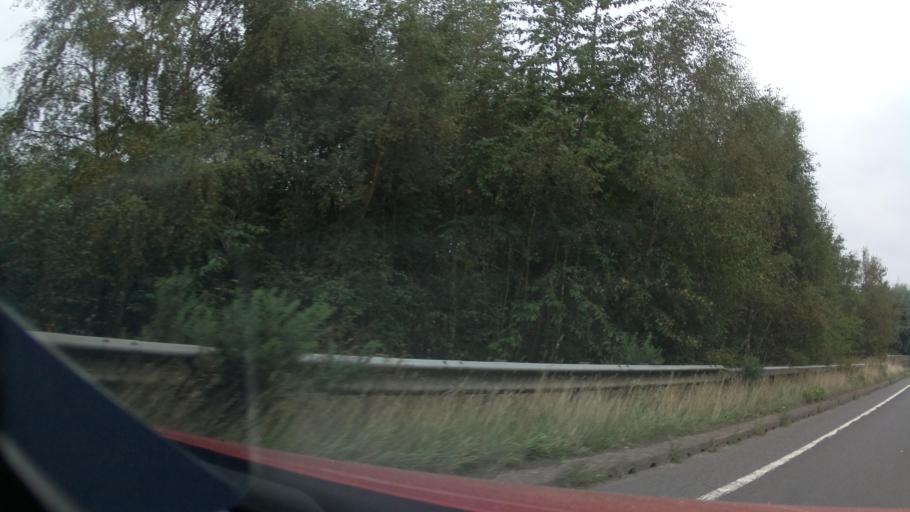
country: GB
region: England
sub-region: Shropshire
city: Stoke upon Tern
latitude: 52.8642
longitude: -2.5554
